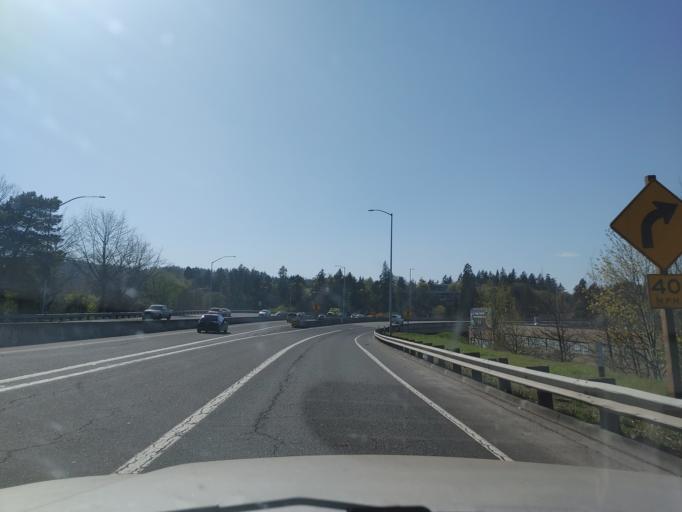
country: US
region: Oregon
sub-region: Clackamas County
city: Milwaukie
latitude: 45.4489
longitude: -122.6393
